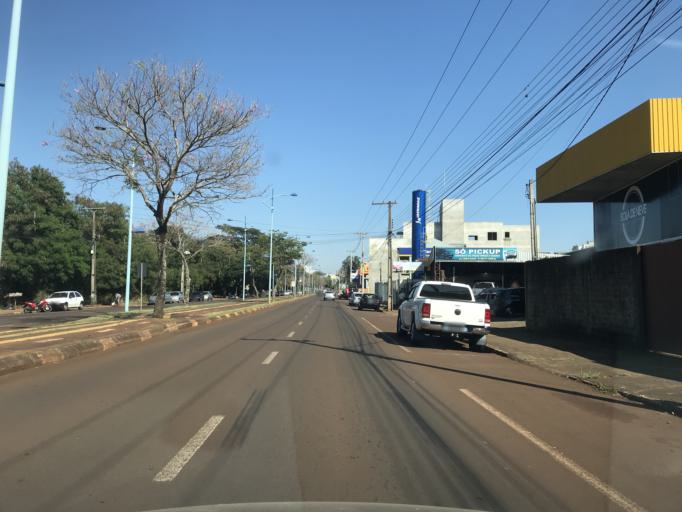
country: BR
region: Parana
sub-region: Toledo
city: Toledo
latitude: -24.7257
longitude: -53.7292
